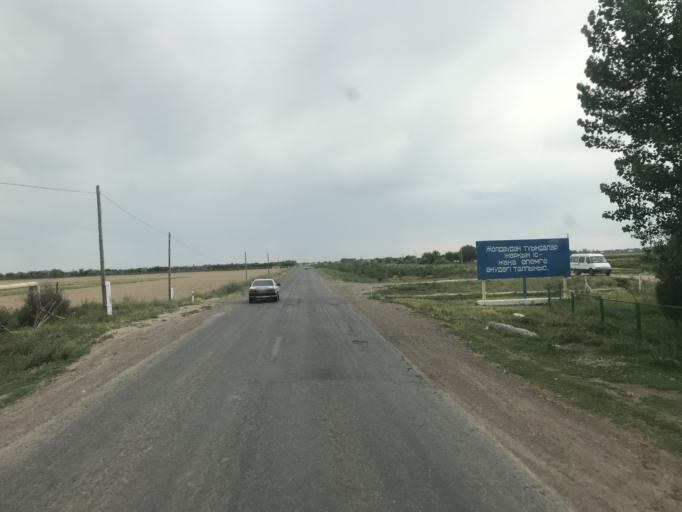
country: KZ
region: Ongtustik Qazaqstan
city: Asykata
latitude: 40.9252
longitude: 68.4030
